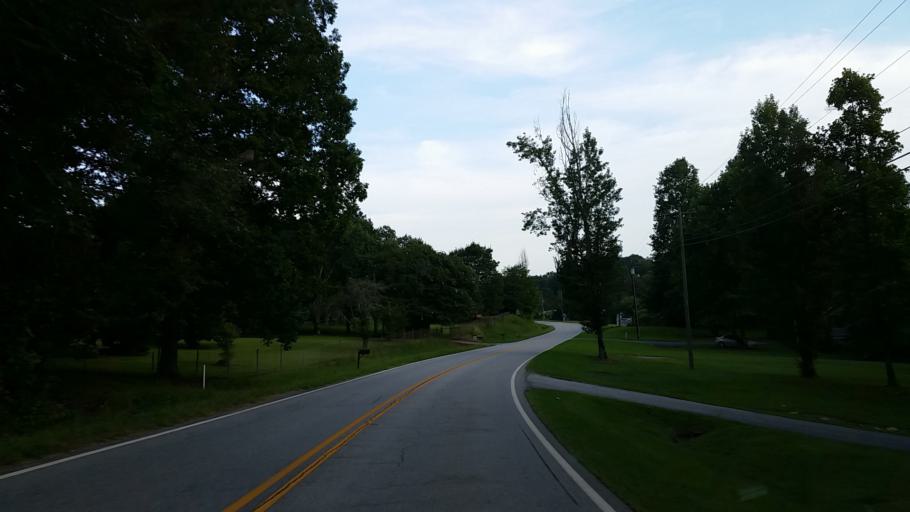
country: US
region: Georgia
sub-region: Lumpkin County
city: Dahlonega
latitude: 34.5703
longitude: -84.0093
